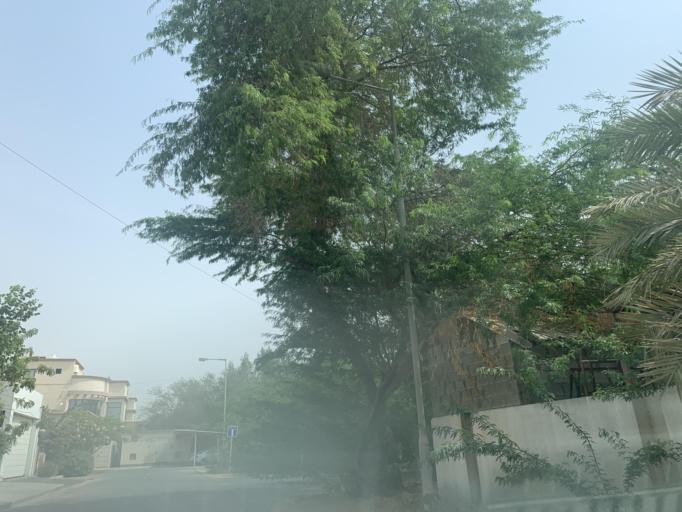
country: BH
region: Manama
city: Jidd Hafs
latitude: 26.2033
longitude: 50.4626
